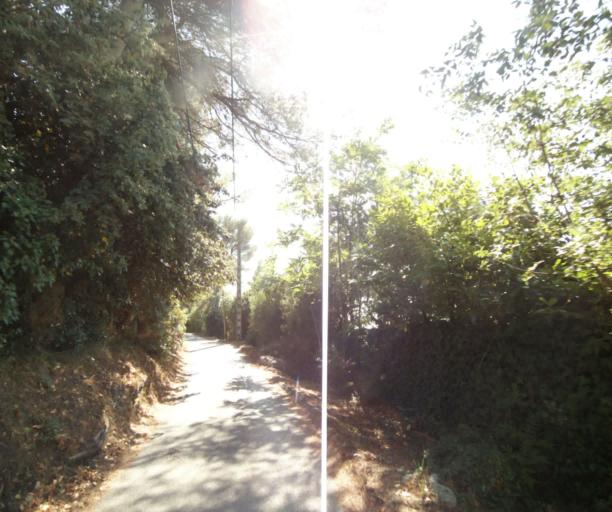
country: FR
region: Provence-Alpes-Cote d'Azur
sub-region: Departement des Alpes-Maritimes
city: Drap
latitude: 43.7531
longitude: 7.3445
